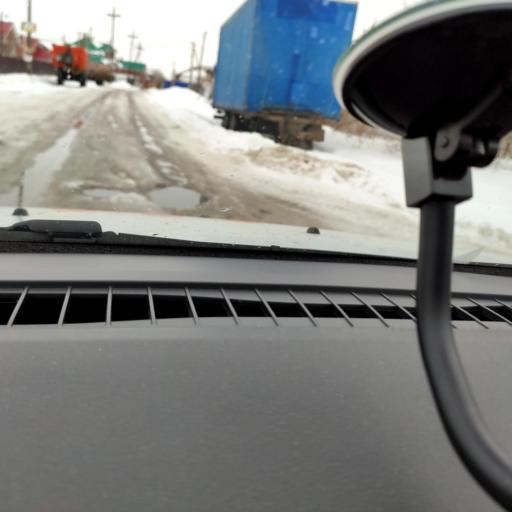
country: RU
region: Samara
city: Samara
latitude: 53.1406
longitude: 50.2428
